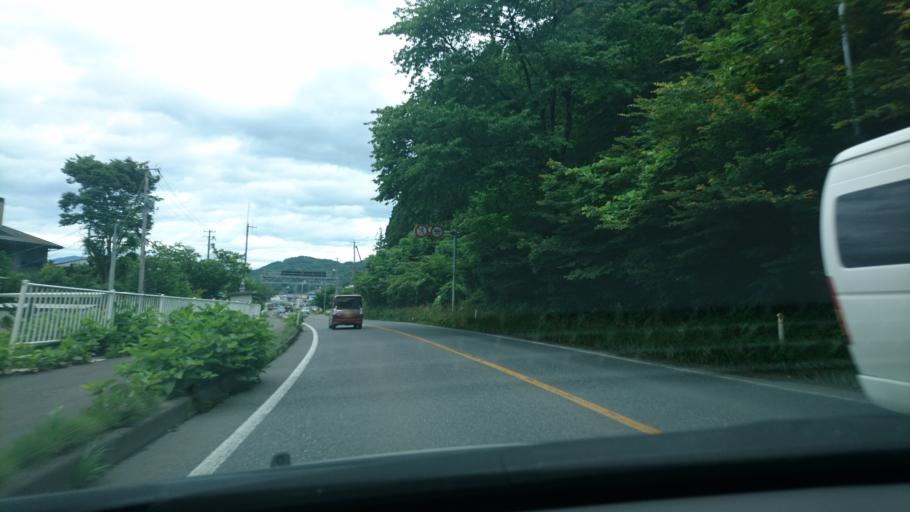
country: JP
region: Iwate
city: Otsuchi
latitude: 39.3659
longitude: 141.9341
